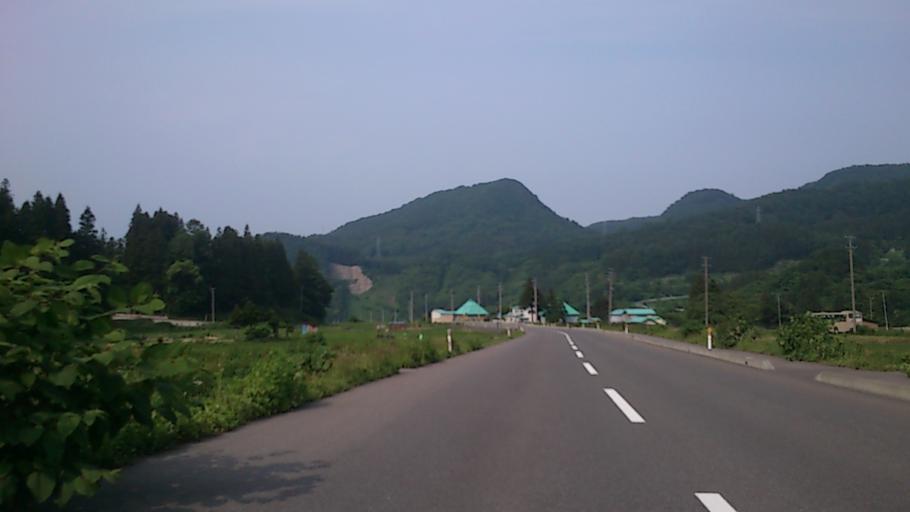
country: JP
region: Aomori
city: Hirosaki
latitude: 40.5500
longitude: 140.2757
